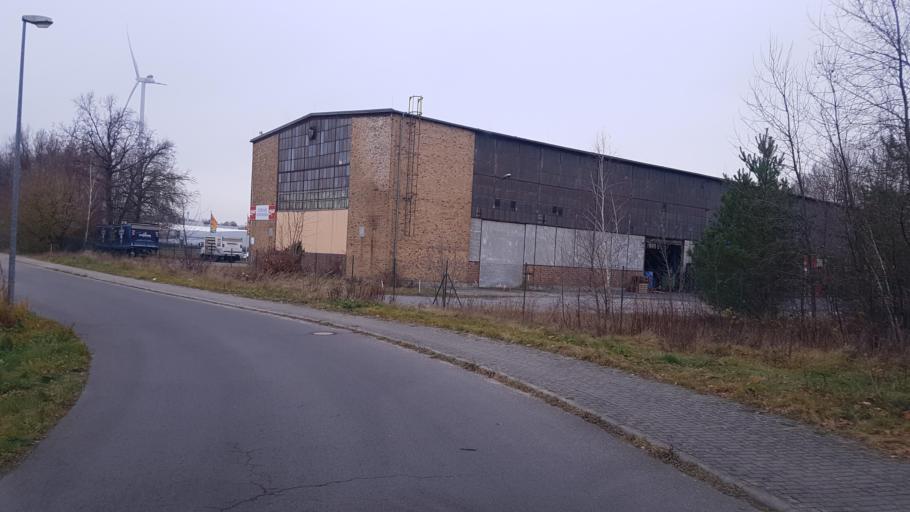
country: DE
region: Brandenburg
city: Lauchhammer
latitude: 51.4731
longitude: 13.7835
